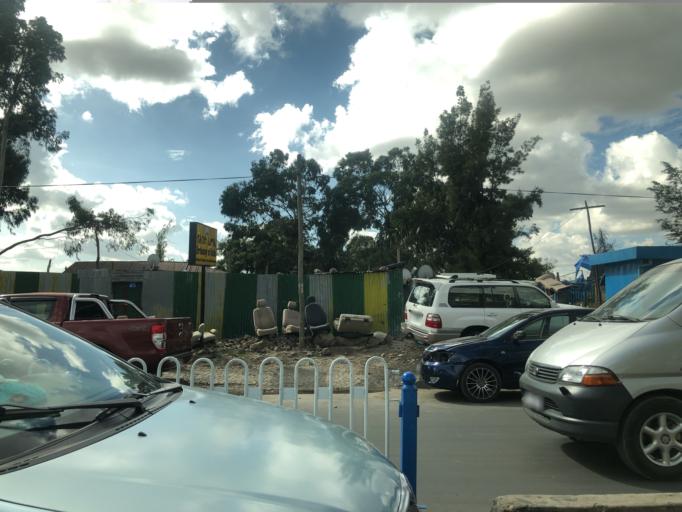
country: ET
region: Adis Abeba
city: Addis Ababa
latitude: 9.0184
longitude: 38.7822
